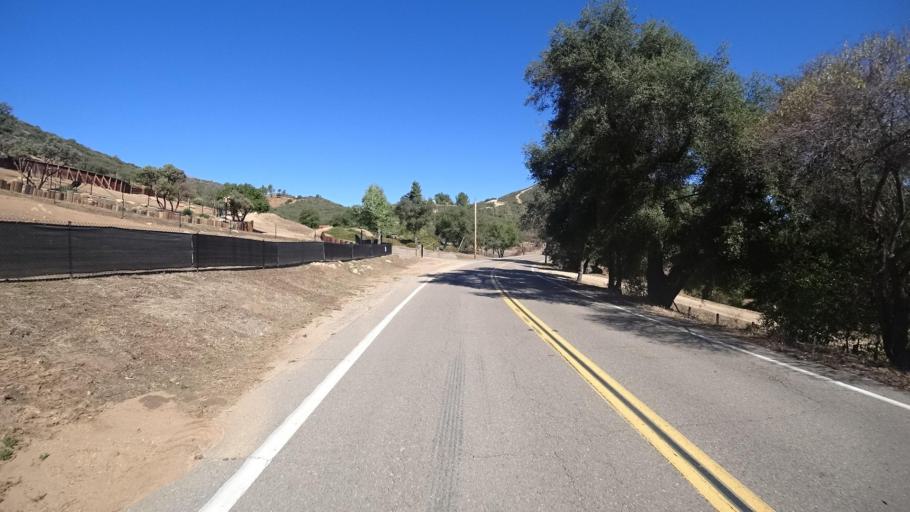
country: US
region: California
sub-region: San Diego County
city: Descanso
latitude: 32.8104
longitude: -116.6354
